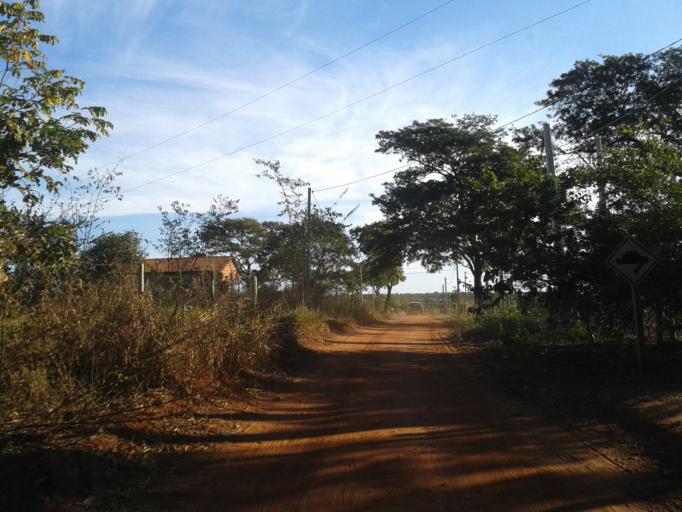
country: BR
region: Minas Gerais
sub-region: Santa Vitoria
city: Santa Vitoria
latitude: -18.9981
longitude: -50.3796
